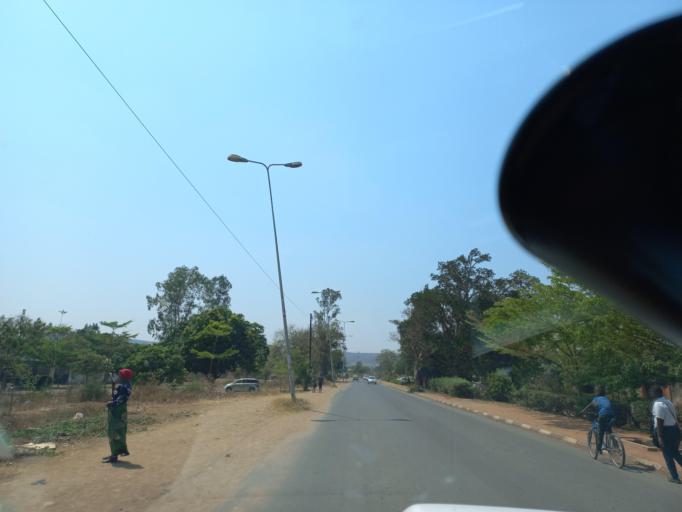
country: ZM
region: Lusaka
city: Kafue
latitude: -15.7435
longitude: 28.1671
